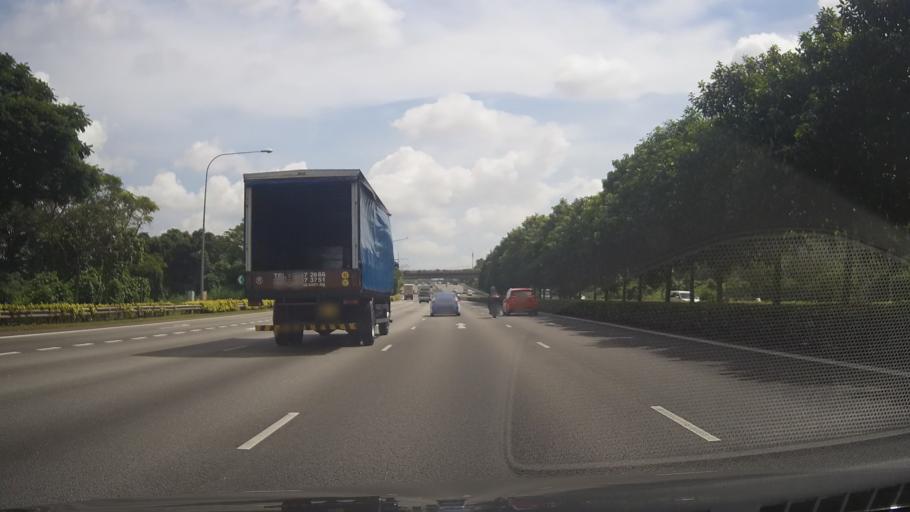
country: MY
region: Johor
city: Kampung Pasir Gudang Baru
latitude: 1.3933
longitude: 103.8295
